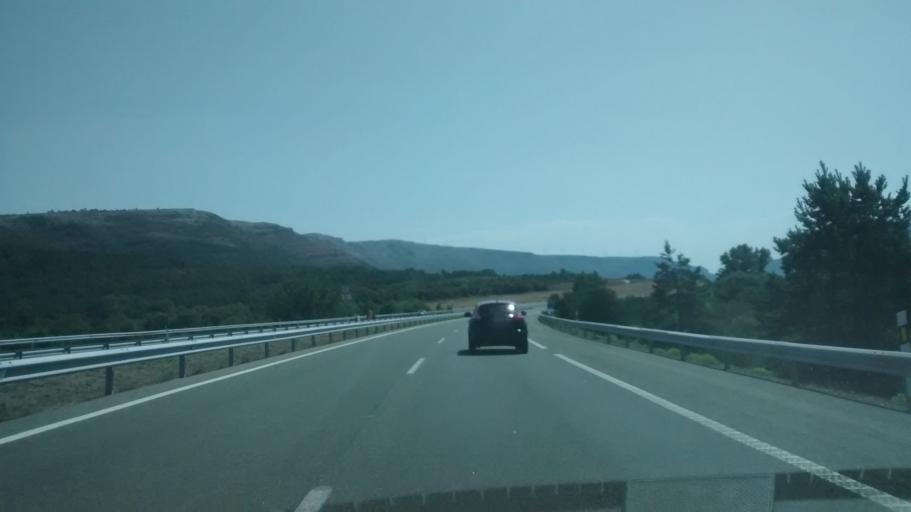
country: ES
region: Basque Country
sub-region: Provincia de Alava
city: Murguia
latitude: 42.9081
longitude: -2.8976
